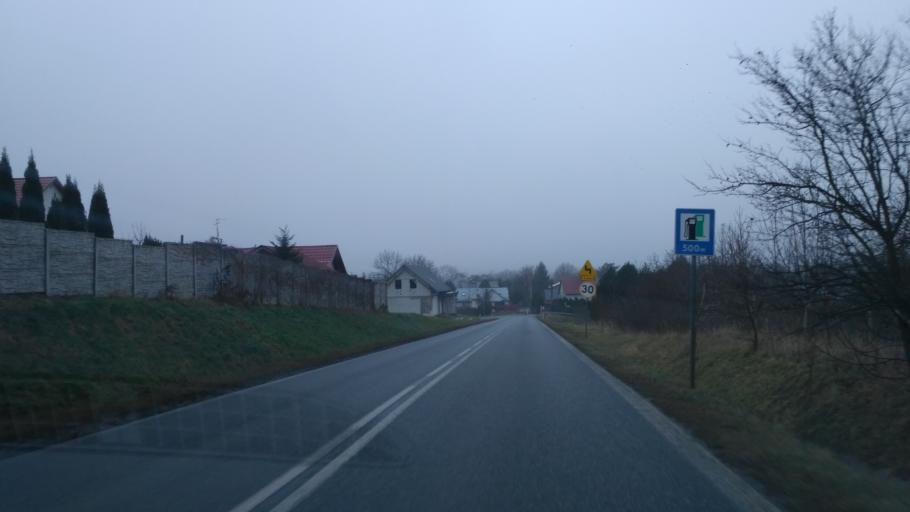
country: PL
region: Subcarpathian Voivodeship
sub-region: Powiat lancucki
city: Sonina
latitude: 50.0563
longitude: 22.2785
